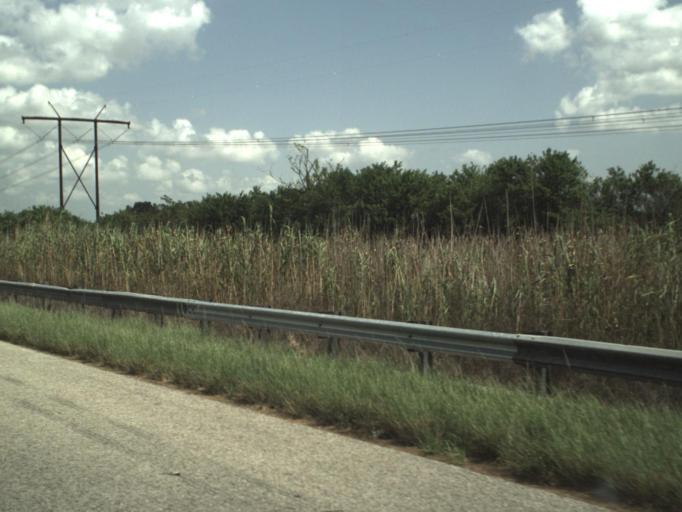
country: US
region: Florida
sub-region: Broward County
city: Weston
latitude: 26.2423
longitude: -80.4662
